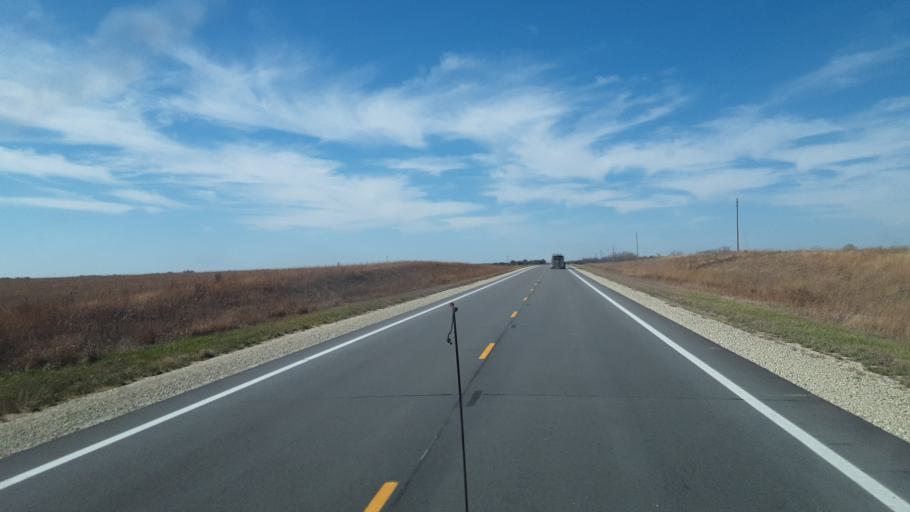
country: US
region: Kansas
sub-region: Marion County
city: Marion
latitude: 38.3629
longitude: -96.8391
